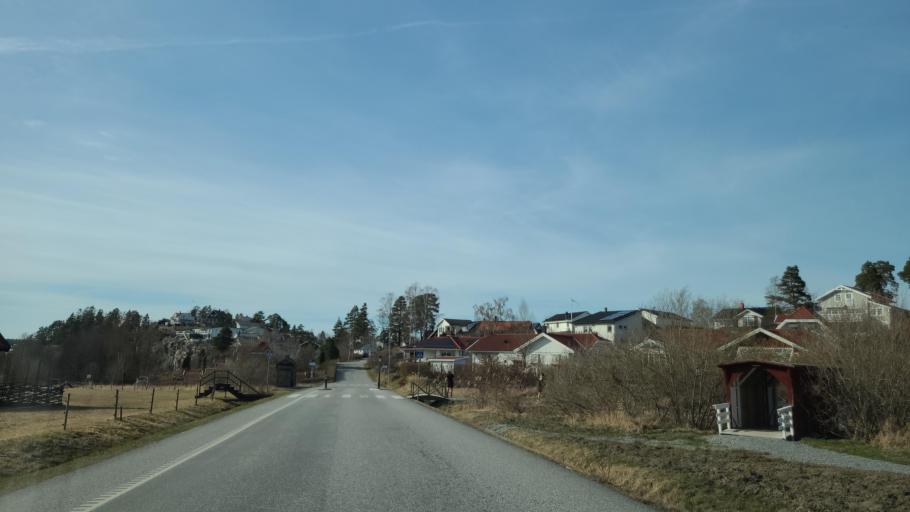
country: SE
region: Stockholm
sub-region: Ekero Kommun
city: Ekeroe
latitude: 59.2869
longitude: 17.7683
